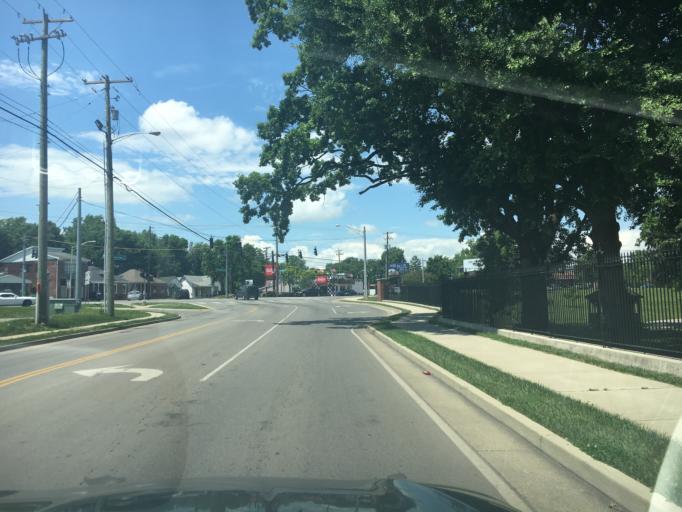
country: US
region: Kentucky
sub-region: Fayette County
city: Mount Vernon
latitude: 38.0597
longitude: -84.5001
